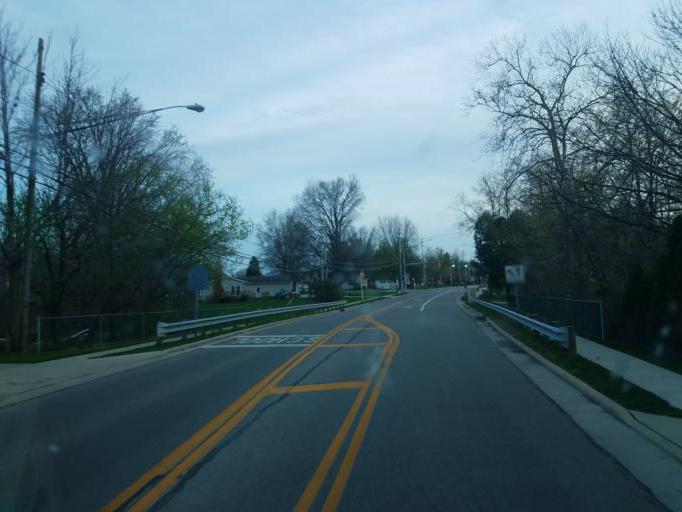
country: US
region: Ohio
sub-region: Lorain County
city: Avon
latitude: 41.4445
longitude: -82.0301
